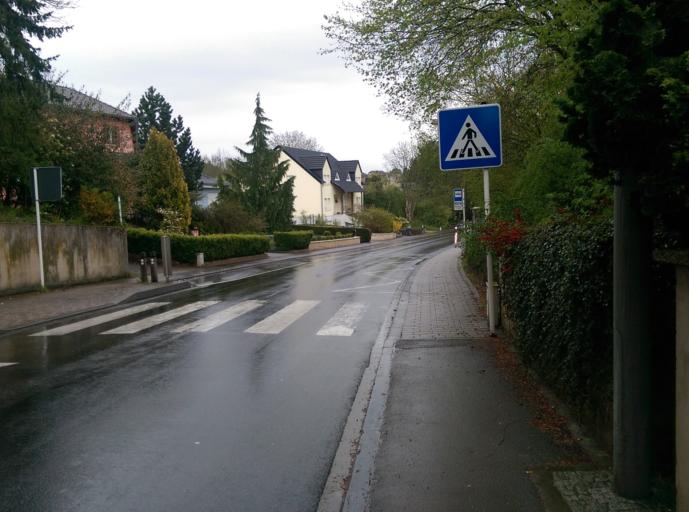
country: LU
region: Luxembourg
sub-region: Canton de Luxembourg
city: Niederanven
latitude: 49.6576
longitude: 6.2438
